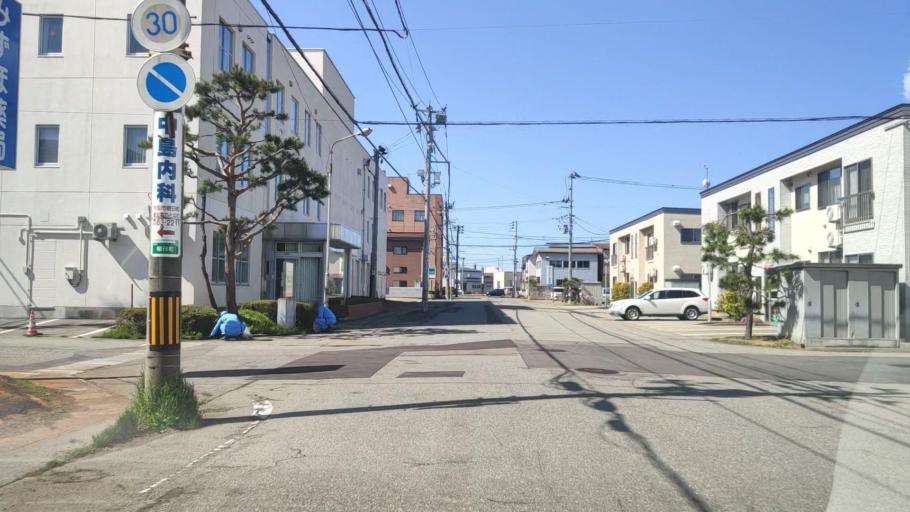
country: JP
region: Akita
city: Omagari
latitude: 39.4686
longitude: 140.4725
